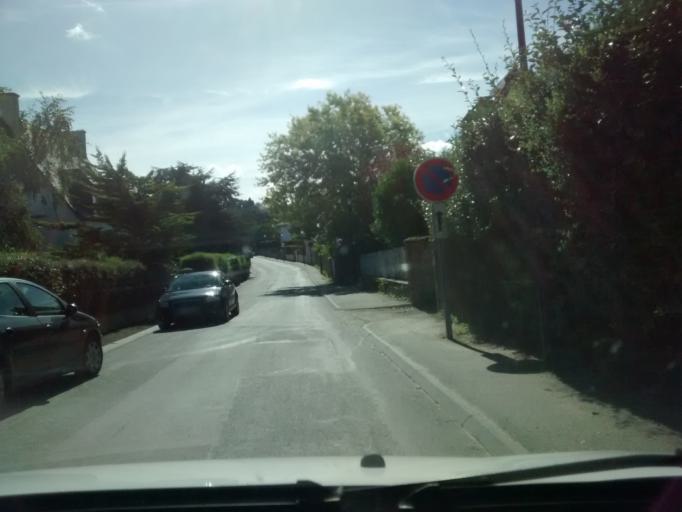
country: FR
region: Brittany
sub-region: Departement d'Ille-et-Vilaine
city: Saint-Briac-sur-Mer
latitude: 48.6265
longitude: -2.1404
